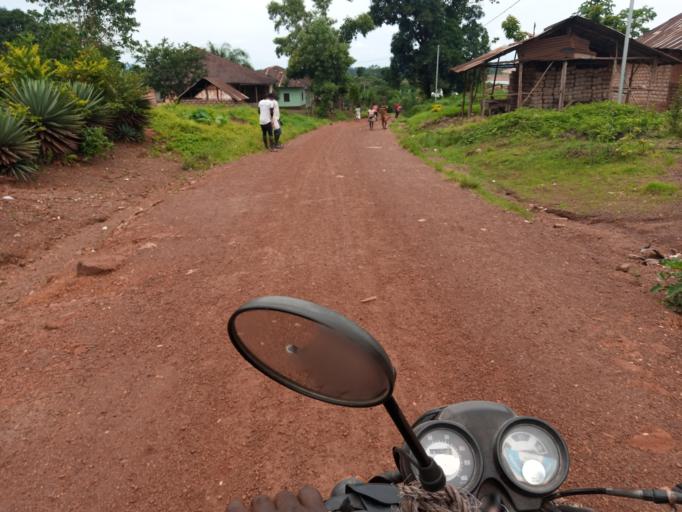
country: SL
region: Southern Province
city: Largo
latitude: 8.2019
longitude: -12.0601
